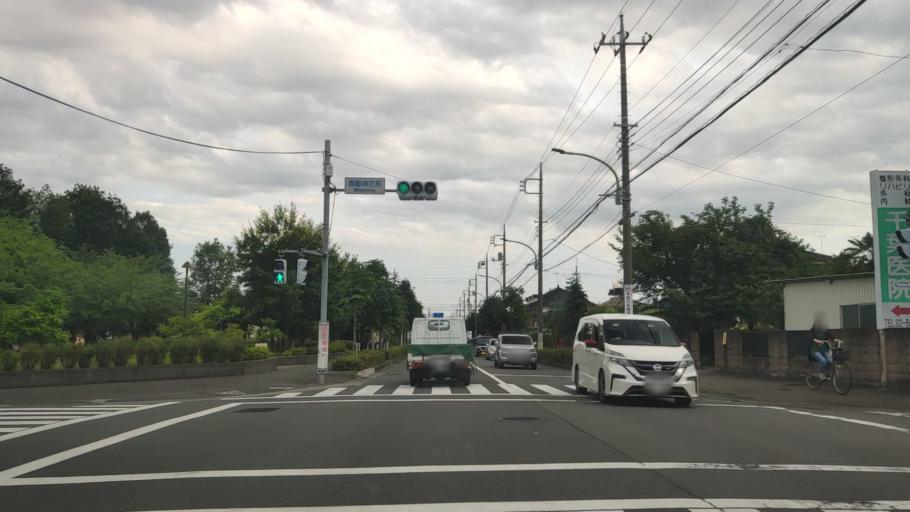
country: JP
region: Tokyo
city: Ome
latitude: 35.7896
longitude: 139.2989
